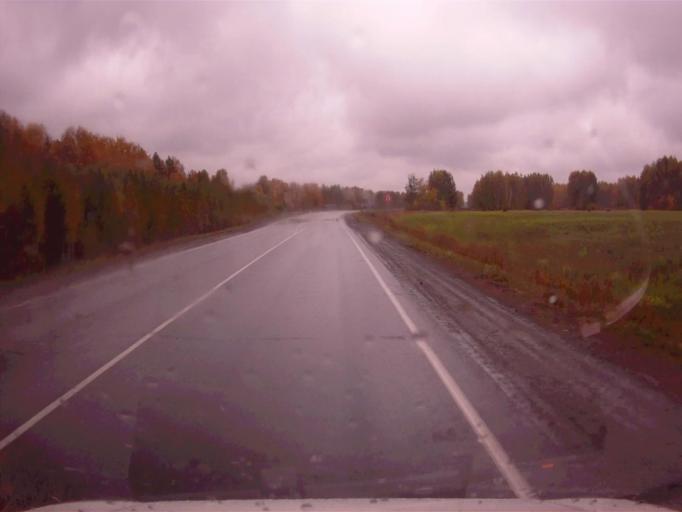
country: RU
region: Chelyabinsk
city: Roshchino
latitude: 55.3993
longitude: 61.0785
